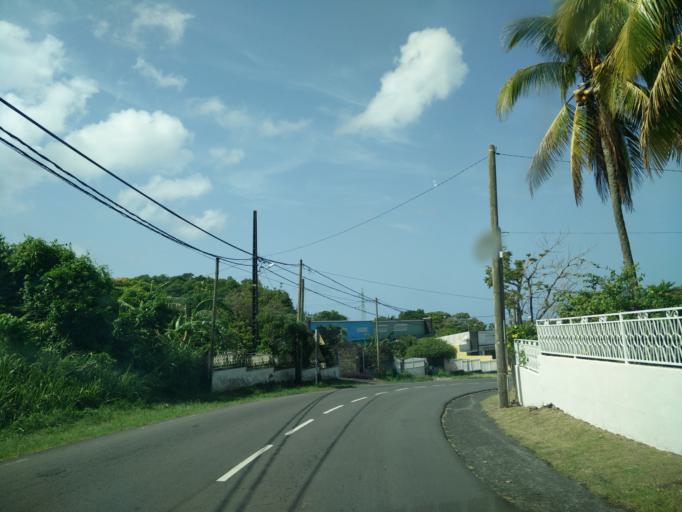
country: GP
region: Guadeloupe
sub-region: Guadeloupe
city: Gourbeyre
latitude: 15.9921
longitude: -61.7058
